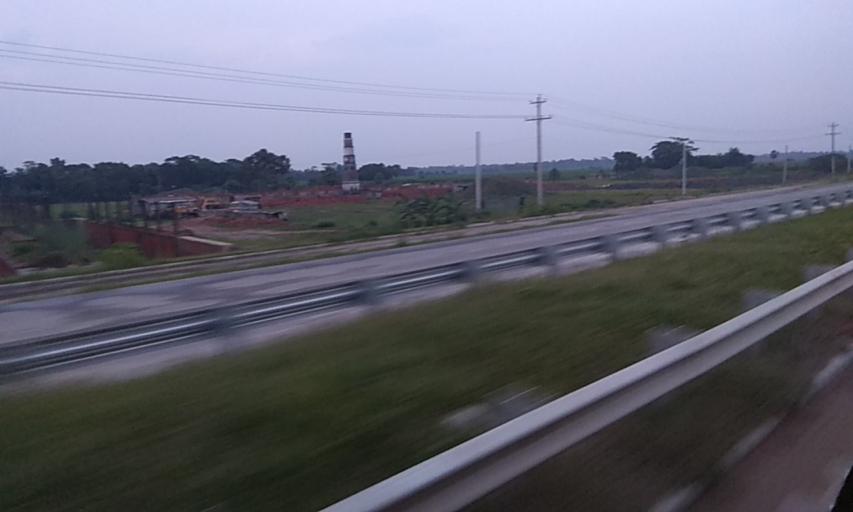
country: BD
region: Dhaka
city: Char Bhadrasan
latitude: 23.3703
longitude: 90.0440
